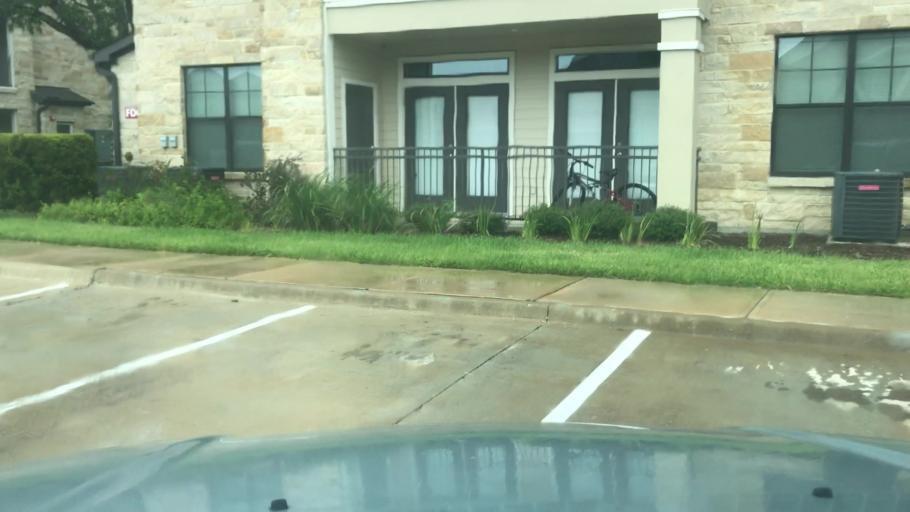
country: US
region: Texas
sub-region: Fort Bend County
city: Cinco Ranch
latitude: 29.7401
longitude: -95.7988
